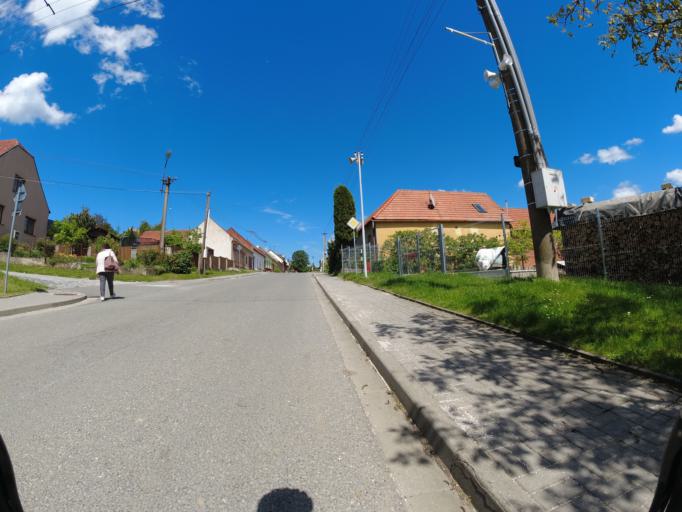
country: CZ
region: Zlin
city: Strani
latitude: 48.9074
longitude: 17.7004
